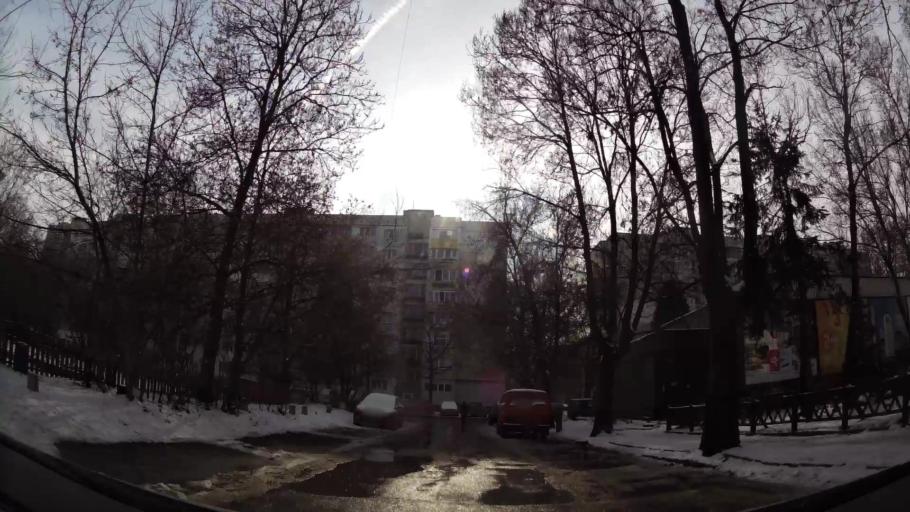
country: BG
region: Sofia-Capital
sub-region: Stolichna Obshtina
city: Sofia
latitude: 42.7060
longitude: 23.3525
